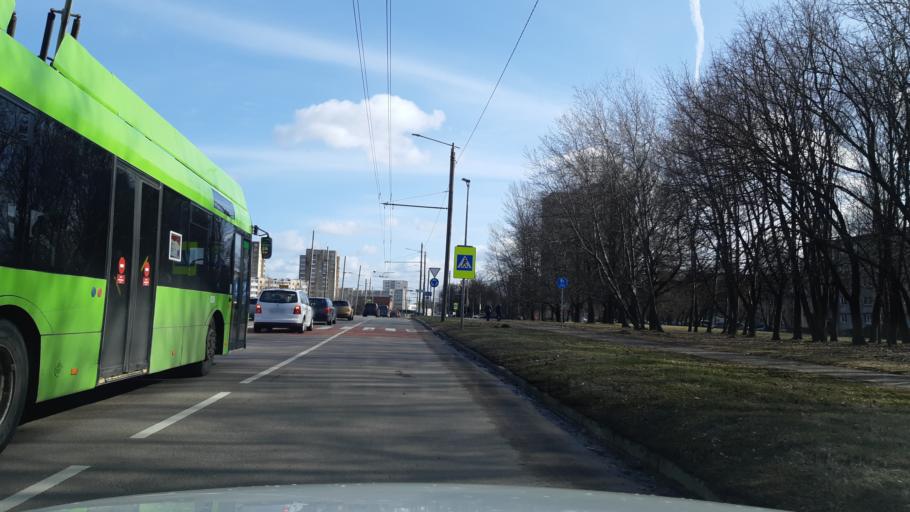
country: LT
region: Kauno apskritis
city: Dainava (Kaunas)
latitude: 54.9117
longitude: 23.9711
